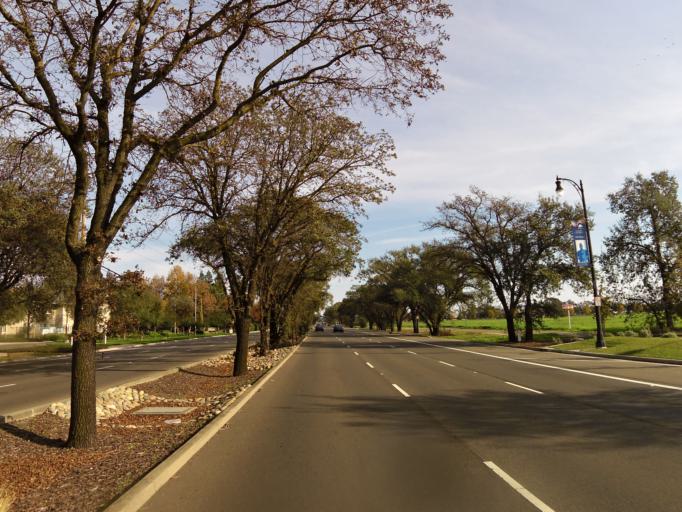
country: US
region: California
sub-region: Sacramento County
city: Laguna
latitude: 38.4090
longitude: -121.3997
